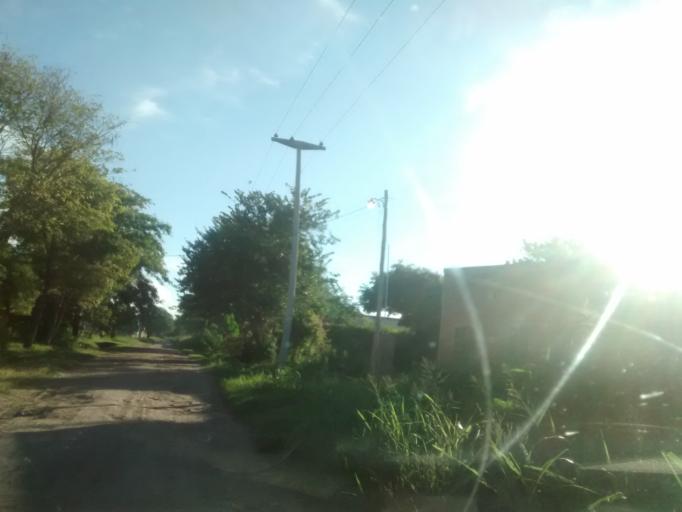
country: AR
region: Chaco
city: Fontana
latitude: -27.4608
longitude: -59.0361
